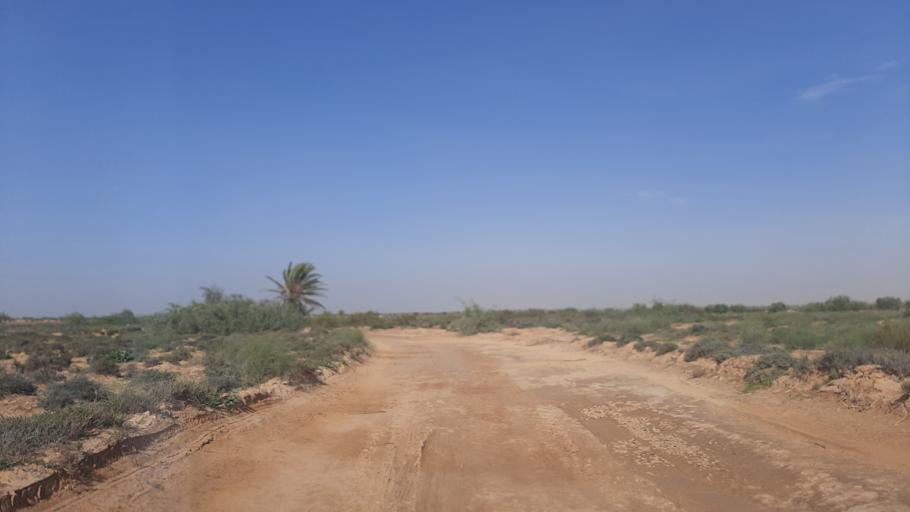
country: TN
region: Madanin
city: Zarzis
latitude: 33.4452
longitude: 10.8082
